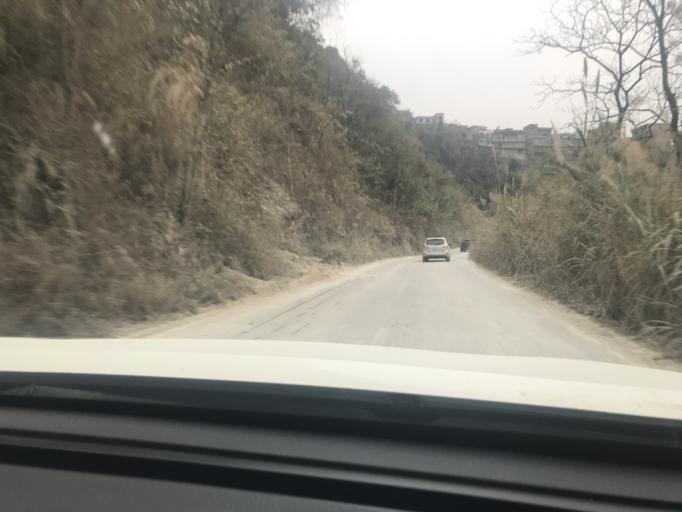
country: CN
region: Guangxi Zhuangzu Zizhiqu
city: Xinzhou
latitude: 24.9881
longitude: 105.8240
